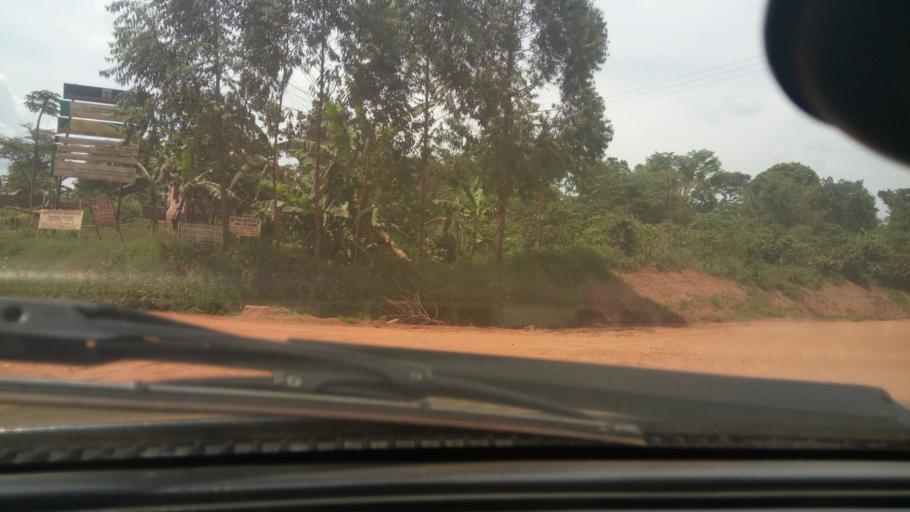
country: UG
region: Central Region
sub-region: Mityana District
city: Mityana
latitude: 0.4249
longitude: 32.0463
